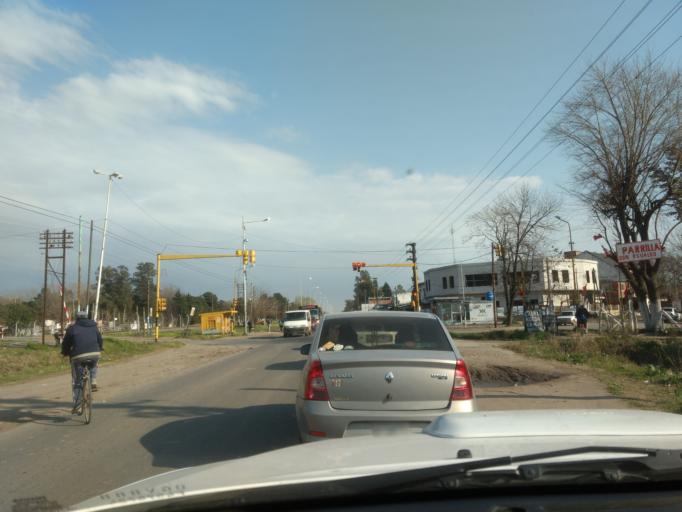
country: AR
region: Buenos Aires
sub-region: Partido de General Rodriguez
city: General Rodriguez
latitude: -34.6255
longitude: -58.8805
